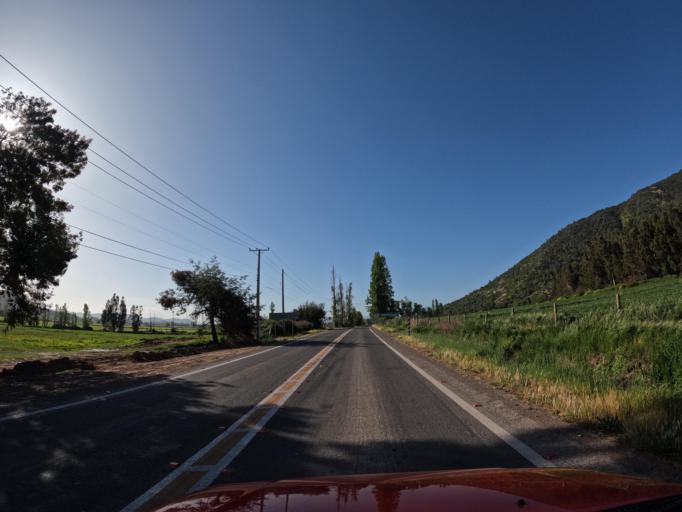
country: CL
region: Maule
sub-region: Provincia de Curico
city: Teno
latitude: -34.7819
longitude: -71.2302
